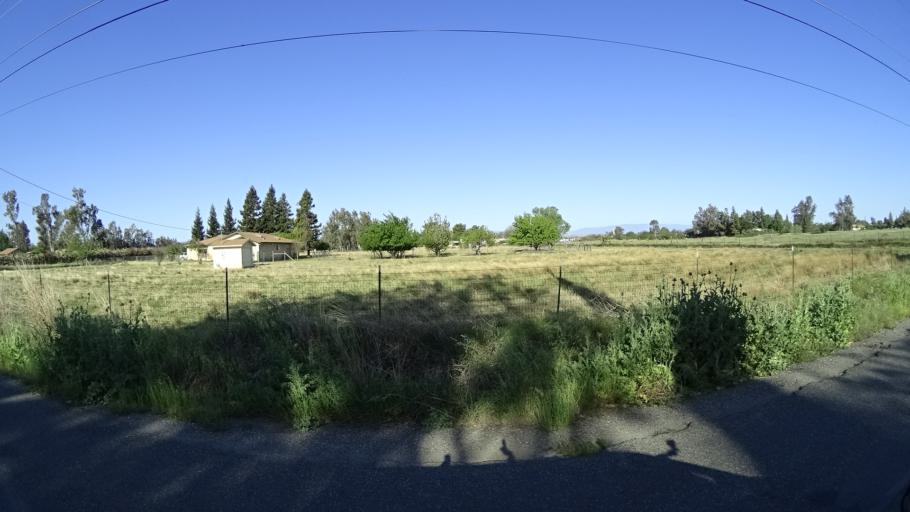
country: US
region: California
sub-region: Glenn County
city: Orland
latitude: 39.7325
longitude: -122.1875
